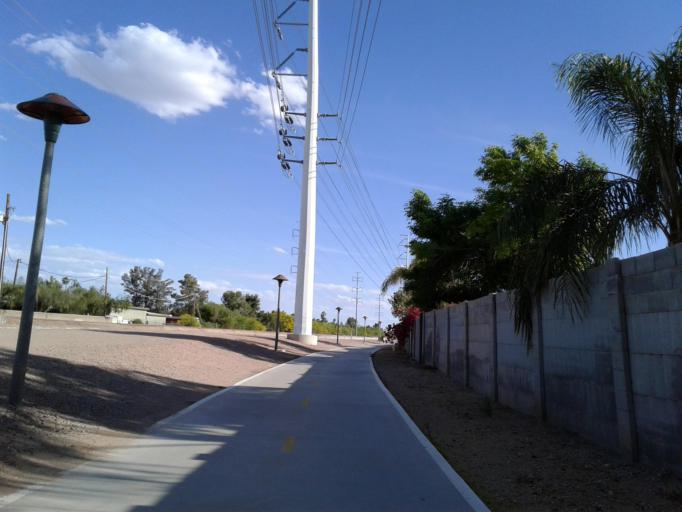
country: US
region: Arizona
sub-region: Maricopa County
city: Scottsdale
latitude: 33.4775
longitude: -111.9405
